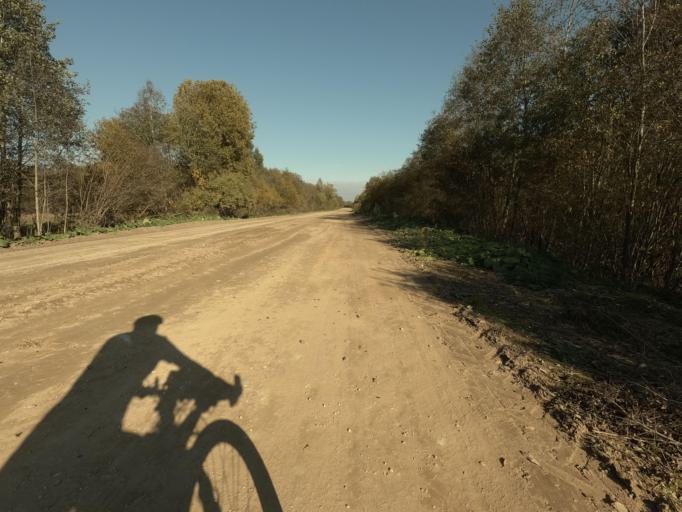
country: RU
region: Novgorod
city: Batetskiy
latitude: 58.8733
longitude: 30.7245
